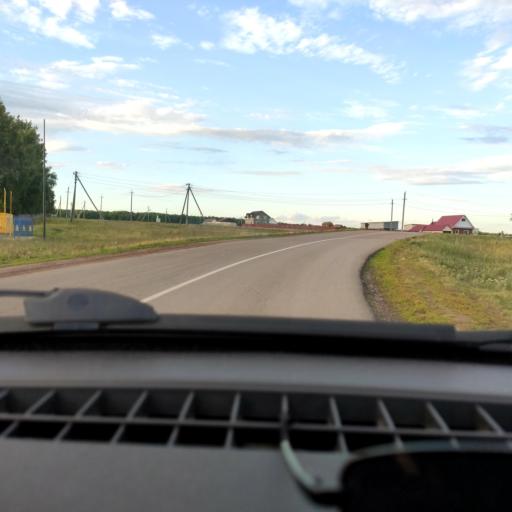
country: RU
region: Bashkortostan
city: Chishmy
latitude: 54.3974
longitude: 55.4615
